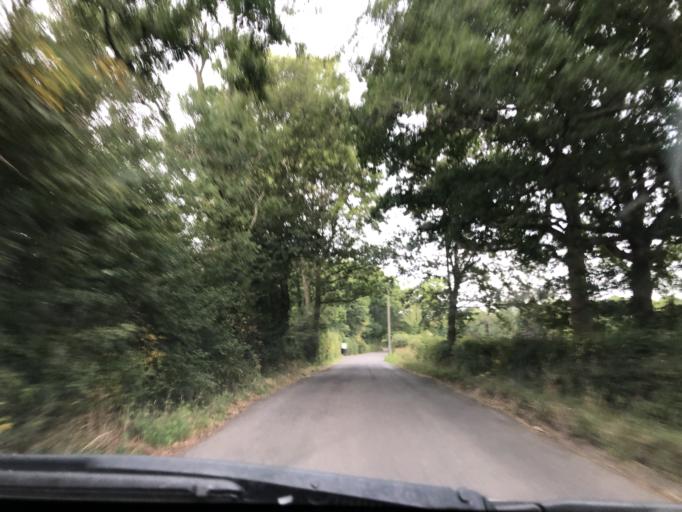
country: GB
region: England
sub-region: Kent
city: Tonbridge
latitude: 51.2323
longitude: 0.2366
